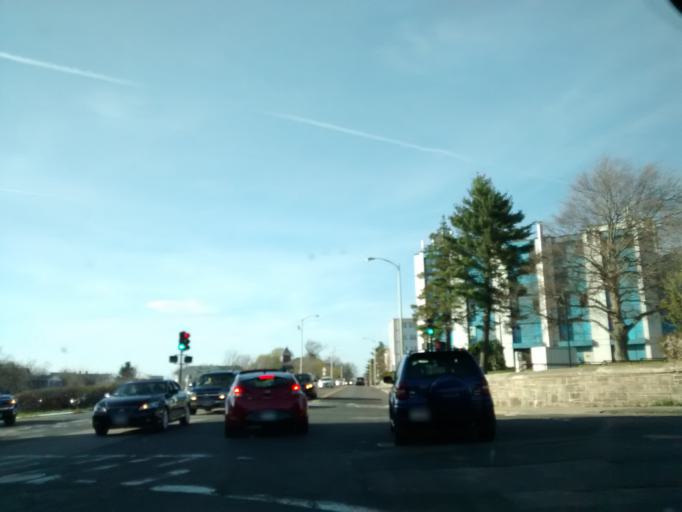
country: US
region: Massachusetts
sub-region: Worcester County
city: Worcester
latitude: 42.2485
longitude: -71.7924
